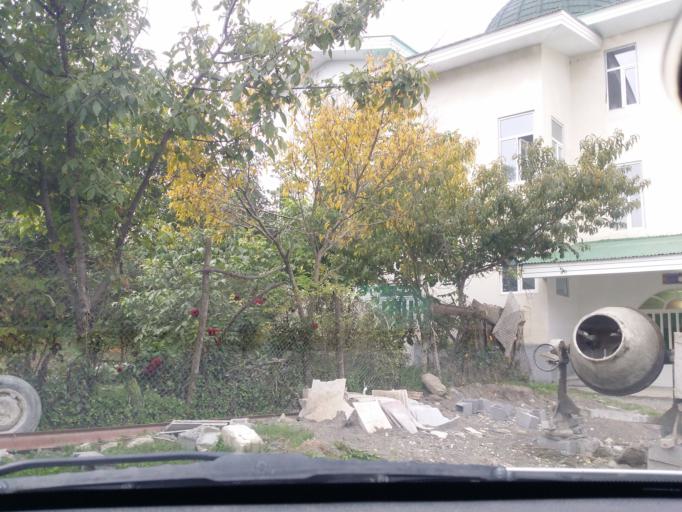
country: IR
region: Mazandaran
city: Chalus
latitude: 36.5098
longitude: 51.2272
